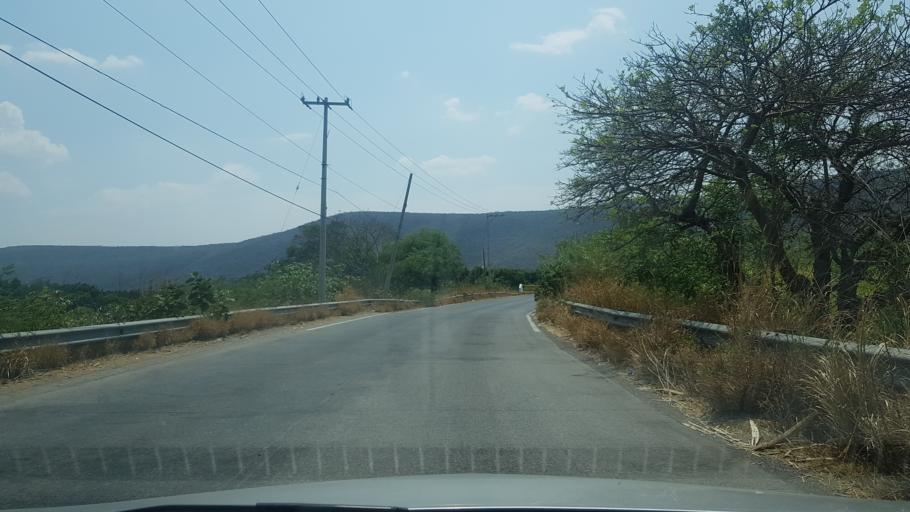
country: MX
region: Morelos
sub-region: Tlaltizapan de Zapata
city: Colonia Palo Prieto (Chipitongo)
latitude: 18.7314
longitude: -99.1185
